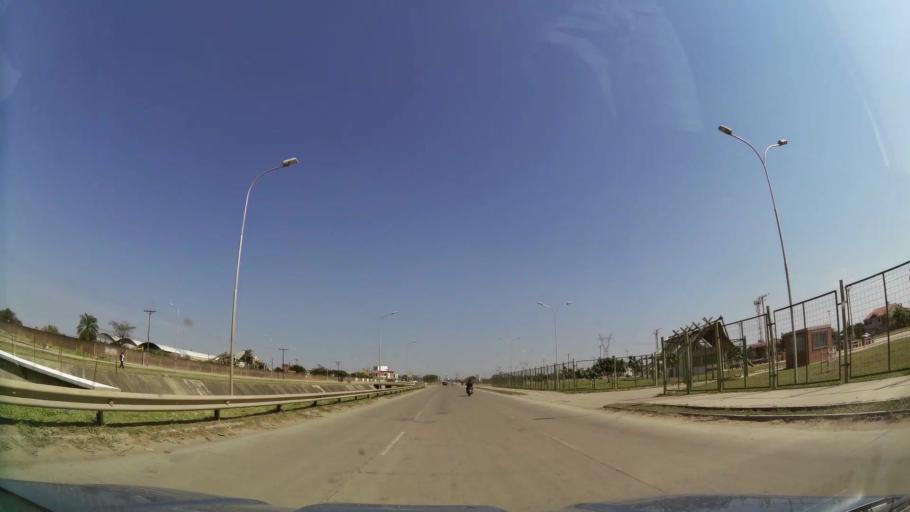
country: BO
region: Santa Cruz
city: Santa Cruz de la Sierra
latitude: -17.7397
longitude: -63.1432
